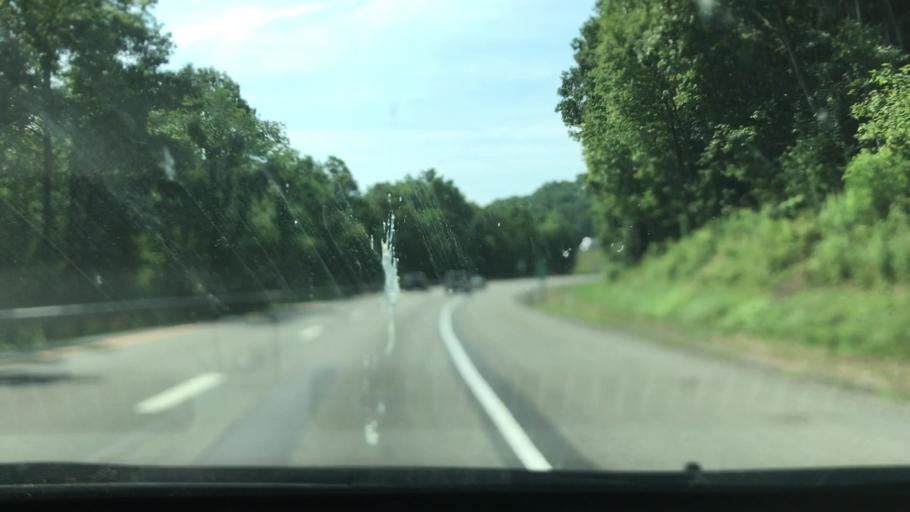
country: US
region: West Virginia
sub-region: Raleigh County
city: Shady Spring
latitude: 37.6722
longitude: -81.1152
